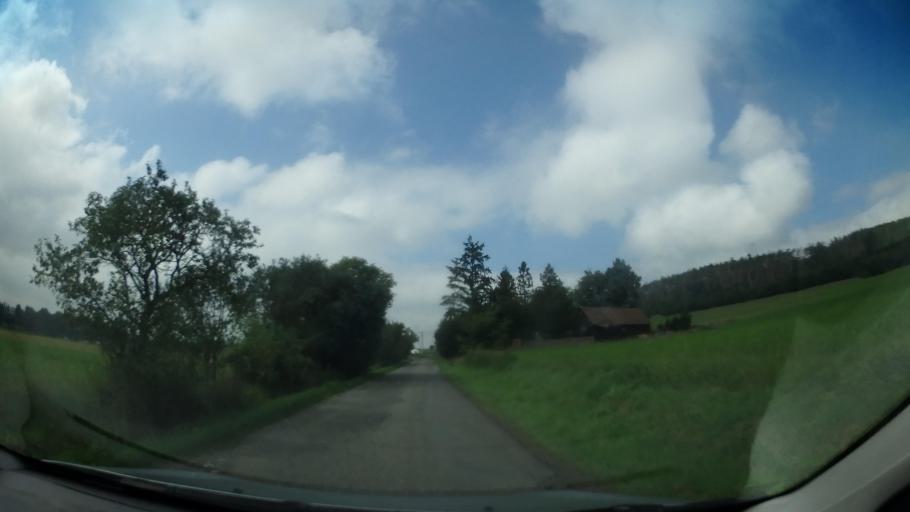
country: CZ
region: Central Bohemia
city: Sedlcany
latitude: 49.7045
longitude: 14.3577
